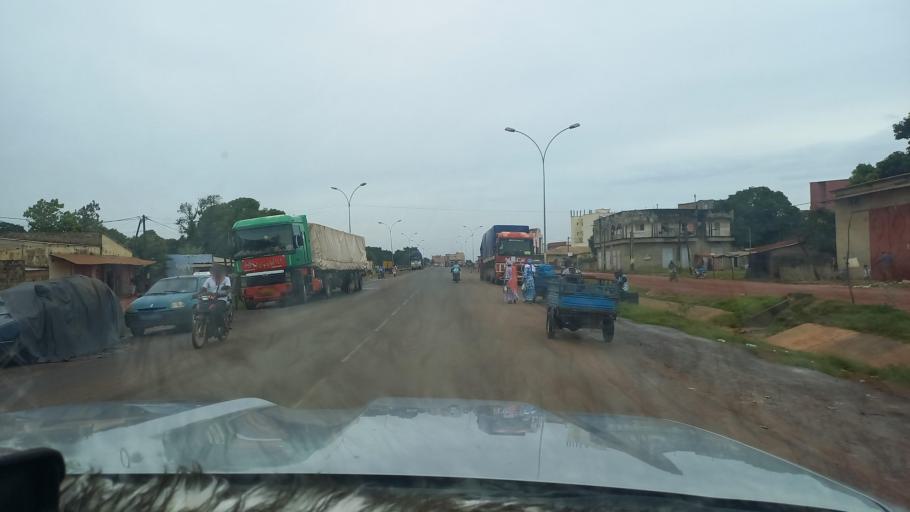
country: SN
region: Ziguinchor
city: Ziguinchor
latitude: 12.5519
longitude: -16.2665
